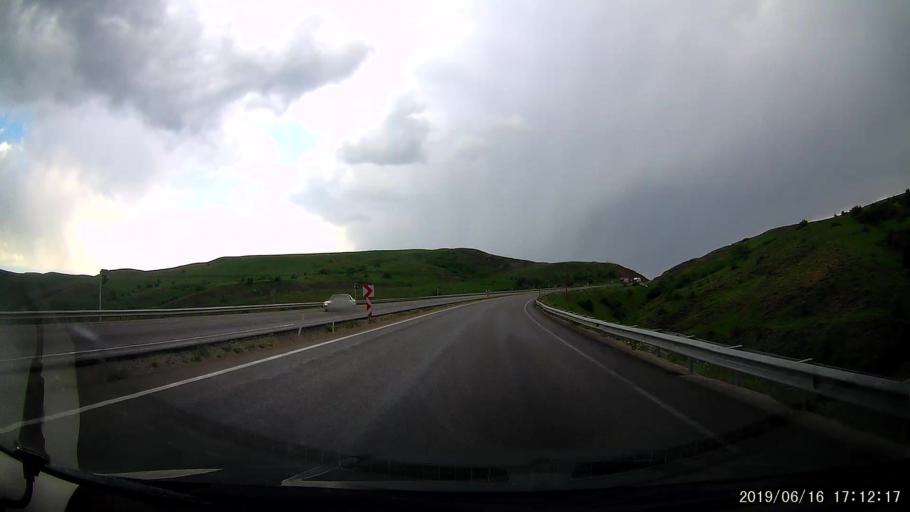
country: TR
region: Erzurum
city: Askale
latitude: 39.8597
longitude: 40.6214
